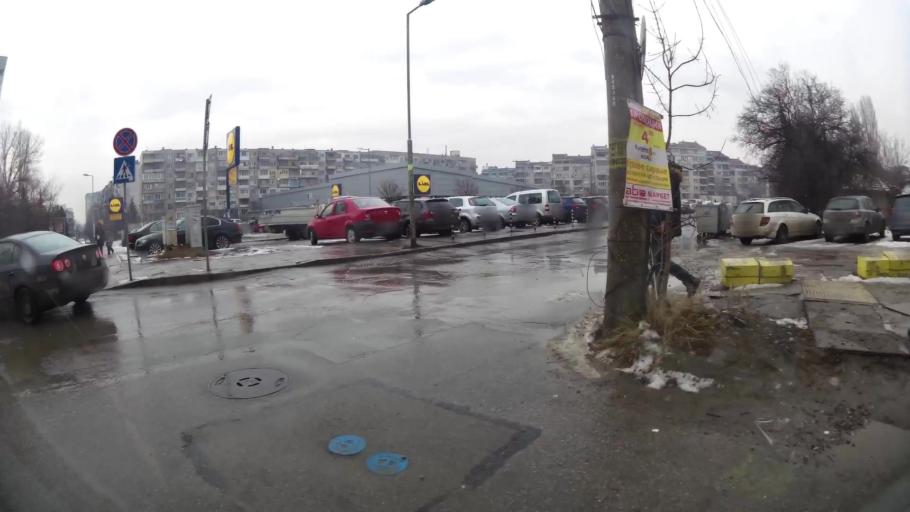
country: BG
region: Sofia-Capital
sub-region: Stolichna Obshtina
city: Sofia
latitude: 42.6594
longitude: 23.2997
